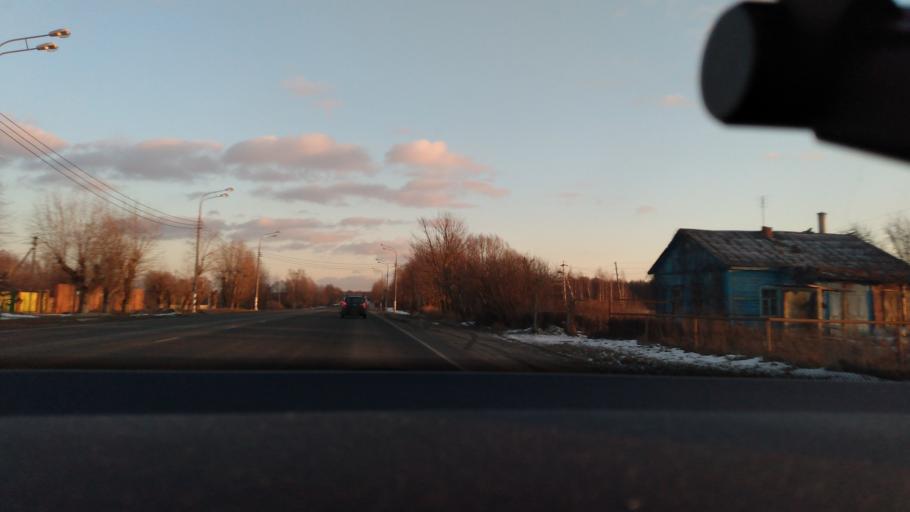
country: RU
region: Moskovskaya
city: Raduzhnyy
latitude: 55.1955
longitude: 38.6199
